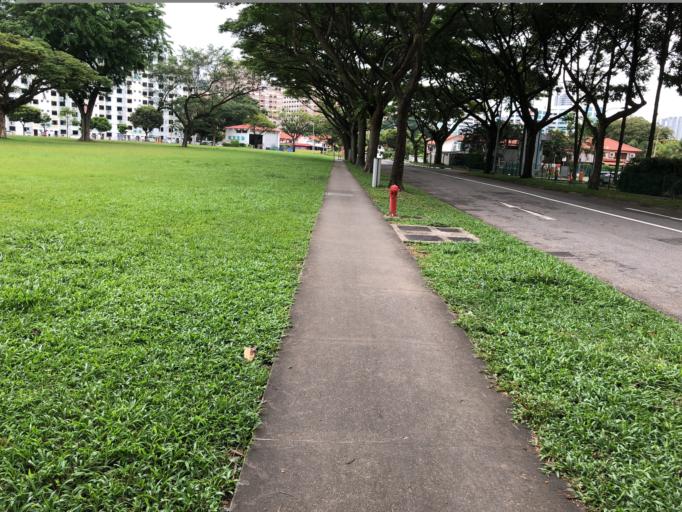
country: SG
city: Singapore
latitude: 1.3283
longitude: 103.8590
